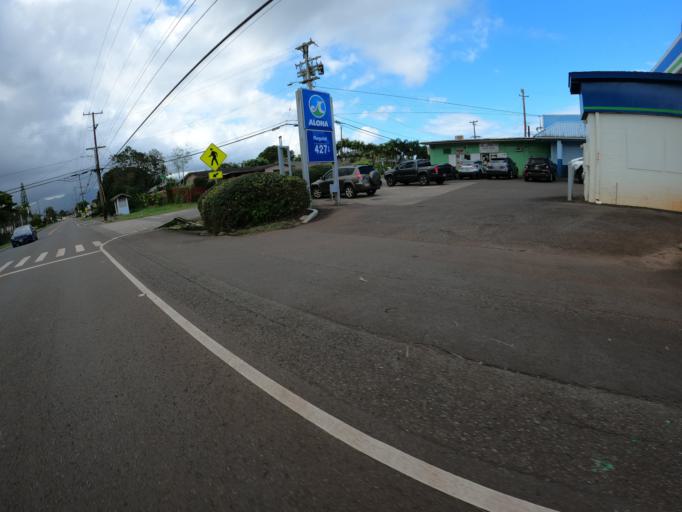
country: US
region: Hawaii
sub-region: Honolulu County
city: Whitmore Village
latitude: 21.5110
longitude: -158.0204
